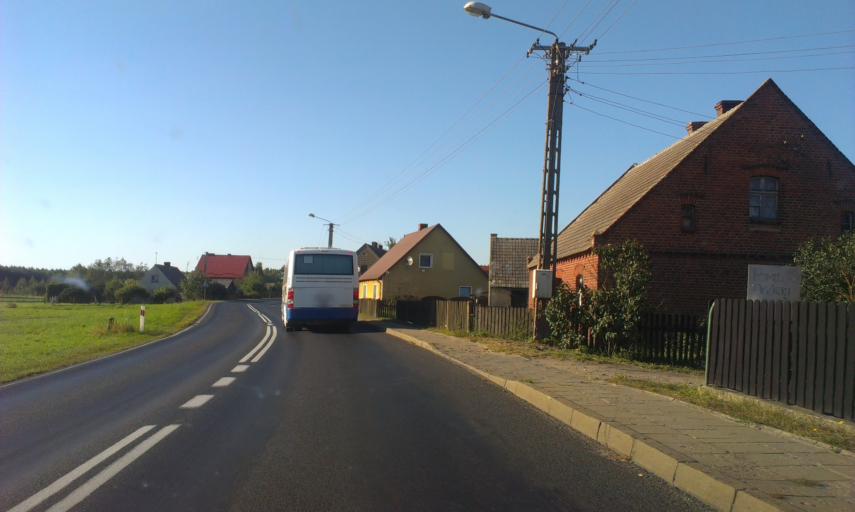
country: PL
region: Kujawsko-Pomorskie
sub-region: Powiat tucholski
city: Cekcyn
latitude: 53.5332
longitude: 17.9440
